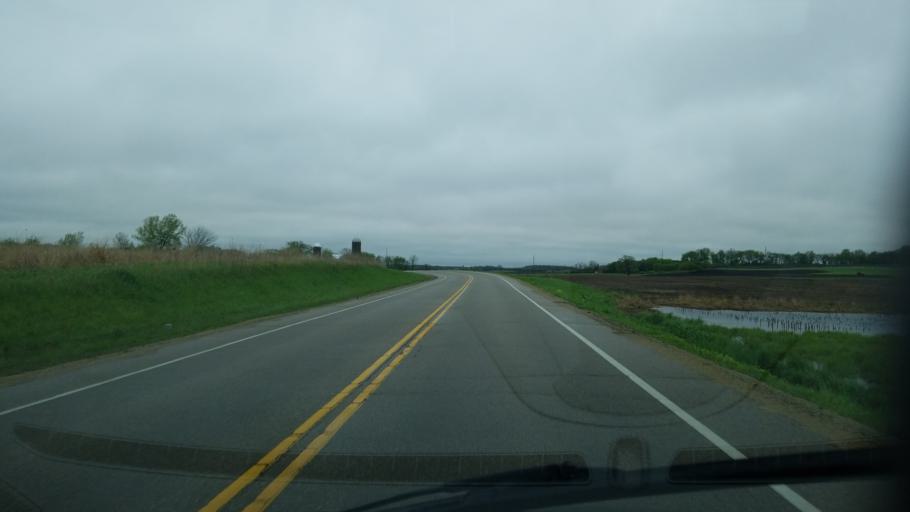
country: US
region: Wisconsin
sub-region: Dane County
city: Fitchburg
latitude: 42.9637
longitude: -89.4366
